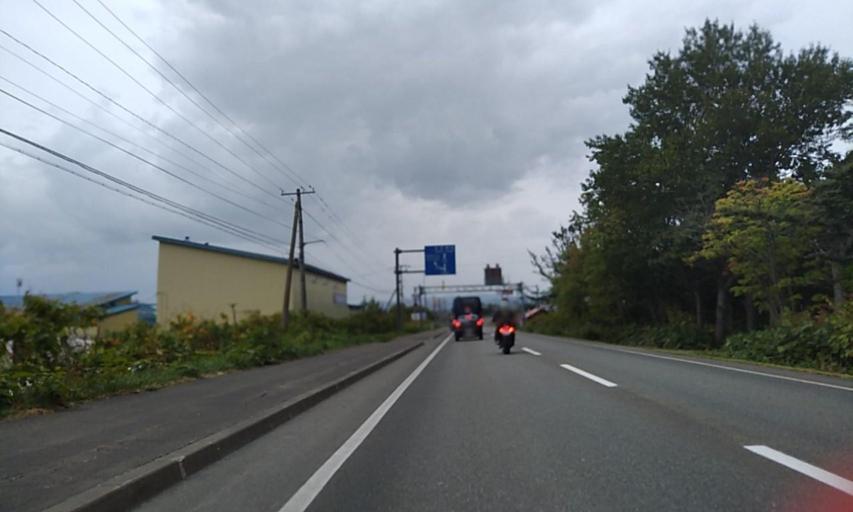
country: JP
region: Hokkaido
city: Nayoro
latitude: 44.9522
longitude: 142.5778
